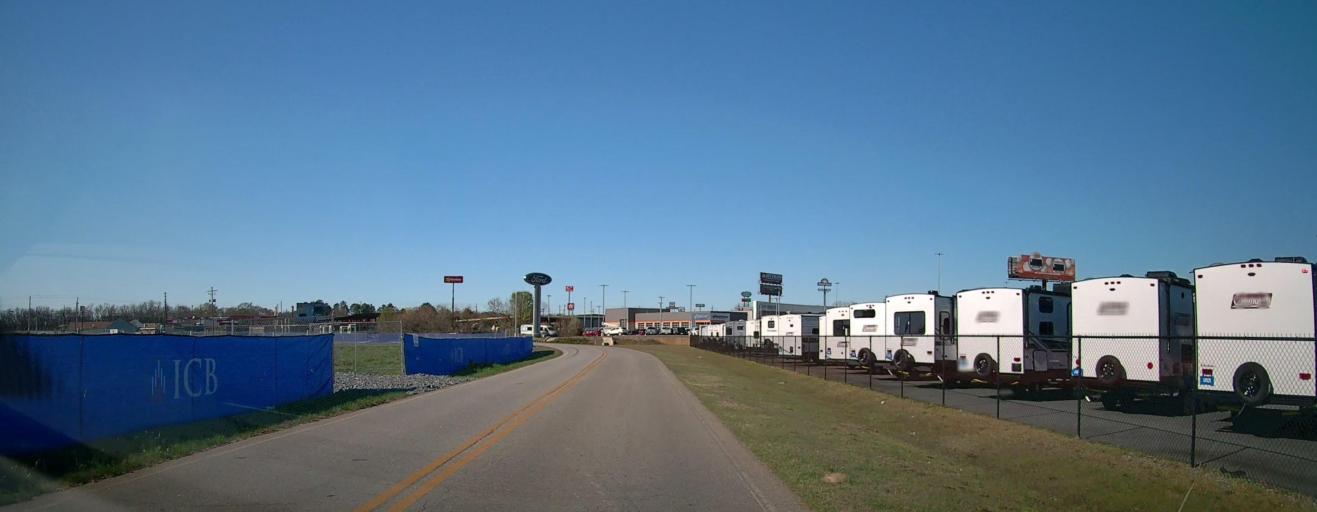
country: US
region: Georgia
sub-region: Peach County
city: Byron
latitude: 32.6544
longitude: -83.7458
